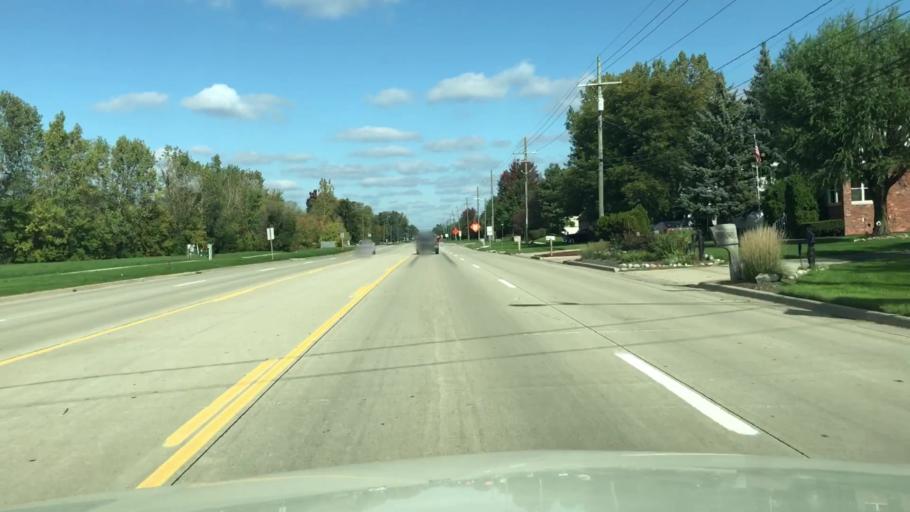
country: US
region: Michigan
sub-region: Macomb County
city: Sterling Heights
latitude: 42.5850
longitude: -83.0895
